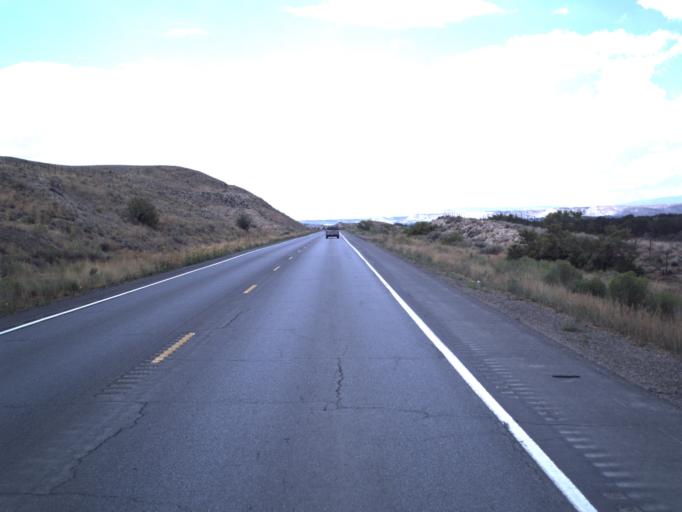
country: US
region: Utah
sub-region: Duchesne County
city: Duchesne
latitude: 40.1555
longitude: -110.2496
